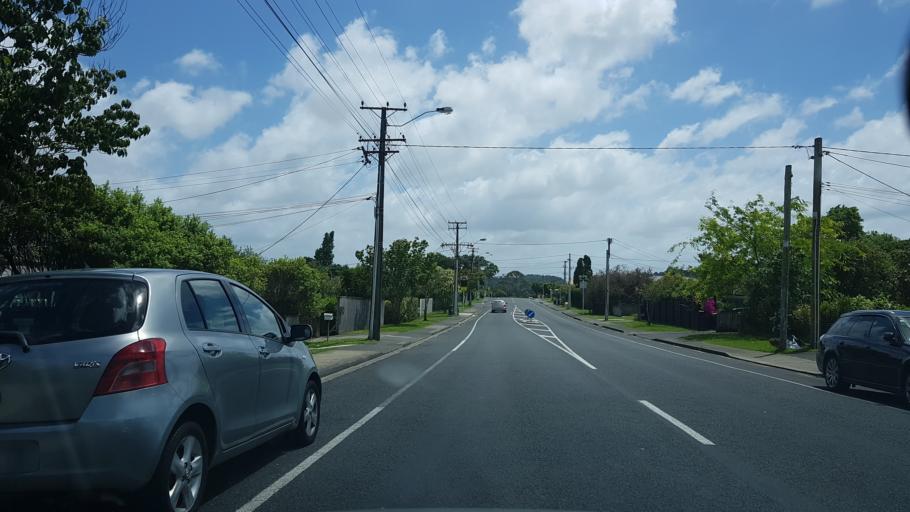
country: NZ
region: Auckland
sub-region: Auckland
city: North Shore
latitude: -36.7942
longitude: 174.7008
